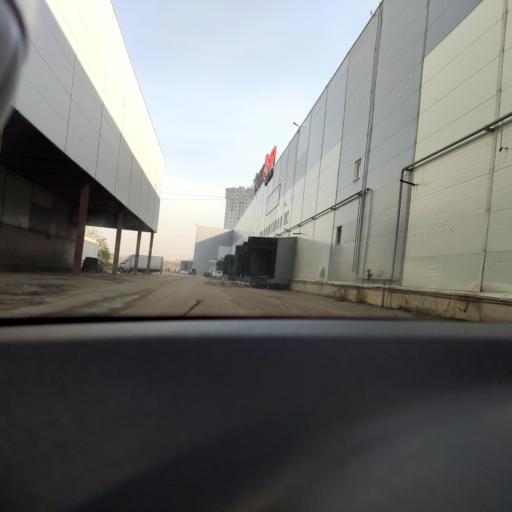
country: RU
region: Samara
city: Petra-Dubrava
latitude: 53.2753
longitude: 50.2733
